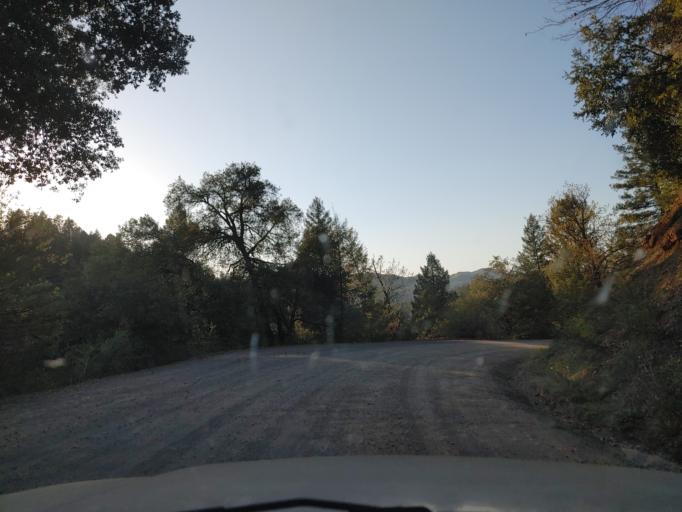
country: US
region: California
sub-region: Shasta County
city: Bella Vista
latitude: 40.8129
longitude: -122.0064
